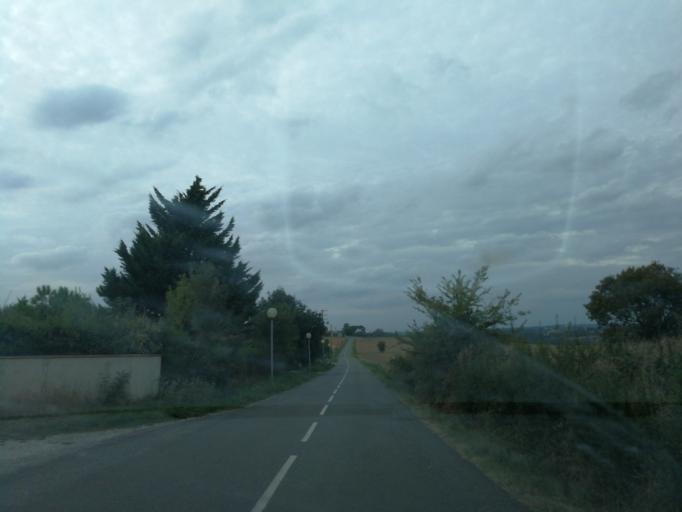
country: FR
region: Midi-Pyrenees
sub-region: Departement de la Haute-Garonne
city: Flourens
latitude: 43.6040
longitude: 1.5455
